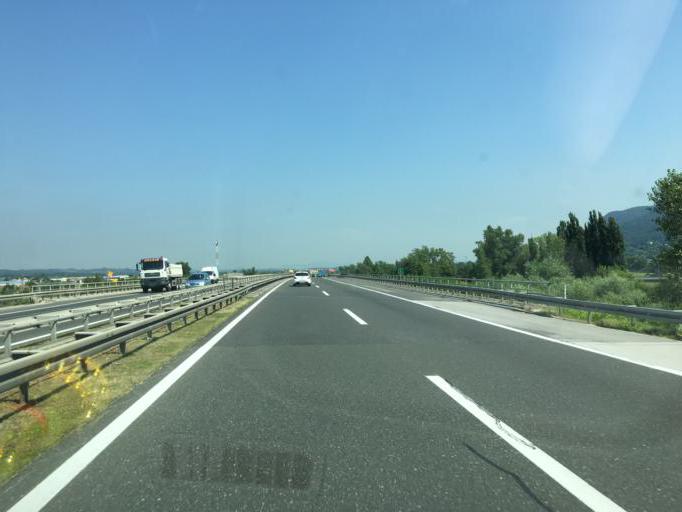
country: HR
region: Zagrebacka
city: Zapresic
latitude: 45.8370
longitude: 15.8194
